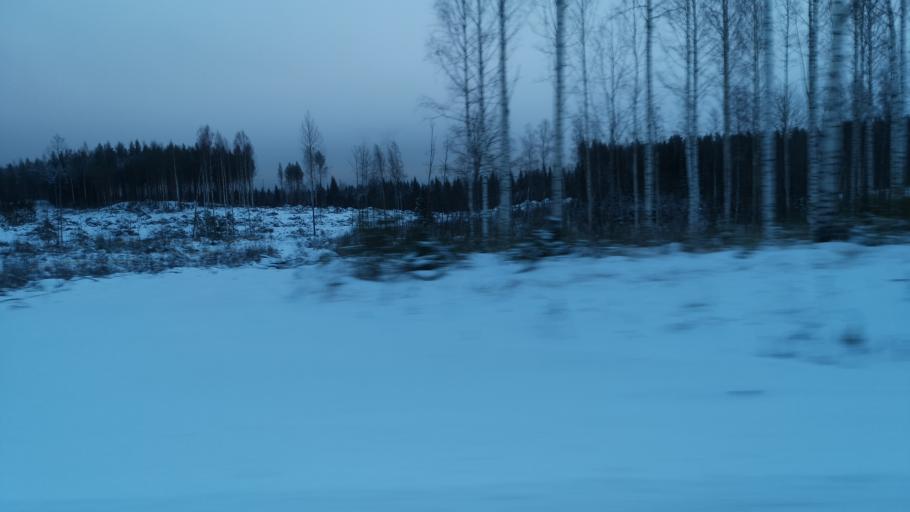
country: FI
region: Southern Savonia
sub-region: Savonlinna
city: Enonkoski
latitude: 62.0915
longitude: 28.6730
